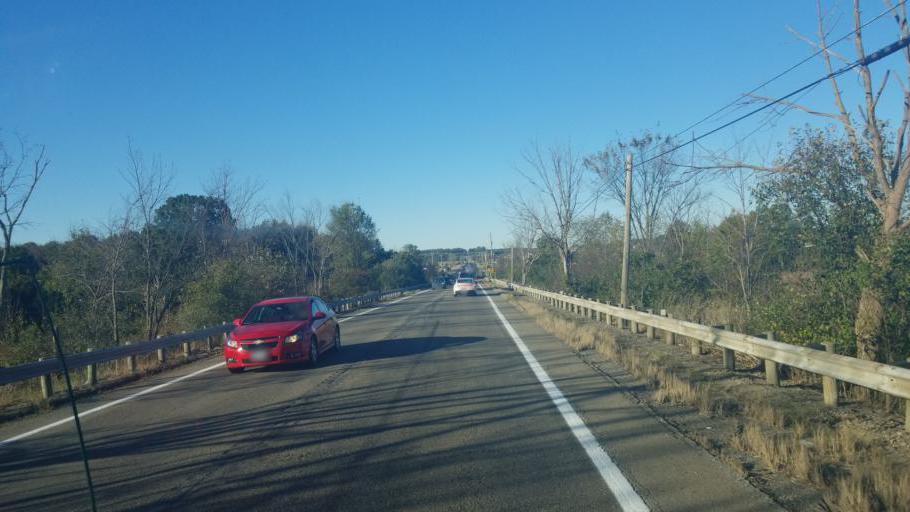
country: US
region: Ohio
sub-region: Columbiana County
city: Columbiana
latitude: 40.8801
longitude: -80.6508
